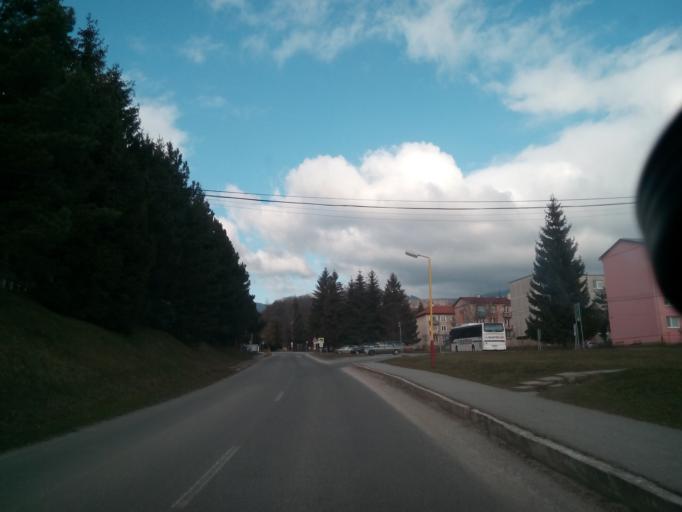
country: SK
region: Kosicky
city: Dobsina
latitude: 48.7172
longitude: 20.2727
